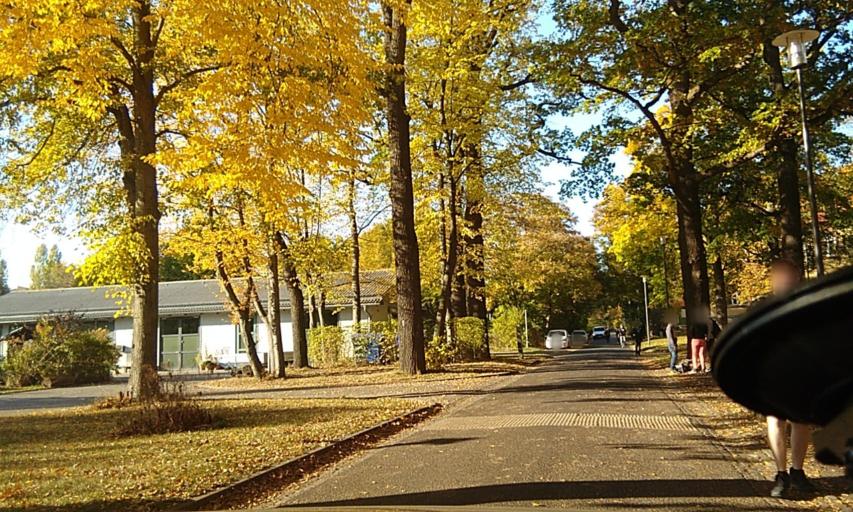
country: DE
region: Saxony
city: Wittgensdorf
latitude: 50.8426
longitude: 12.8743
